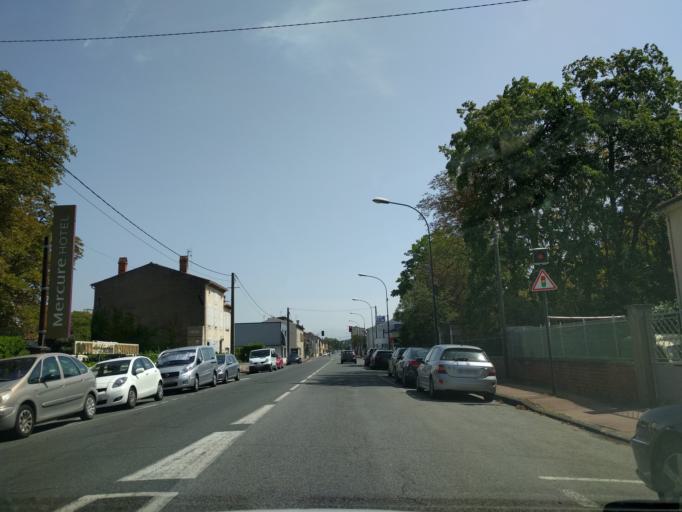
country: FR
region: Midi-Pyrenees
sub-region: Departement du Tarn
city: Castres
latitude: 43.5992
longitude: 2.2567
